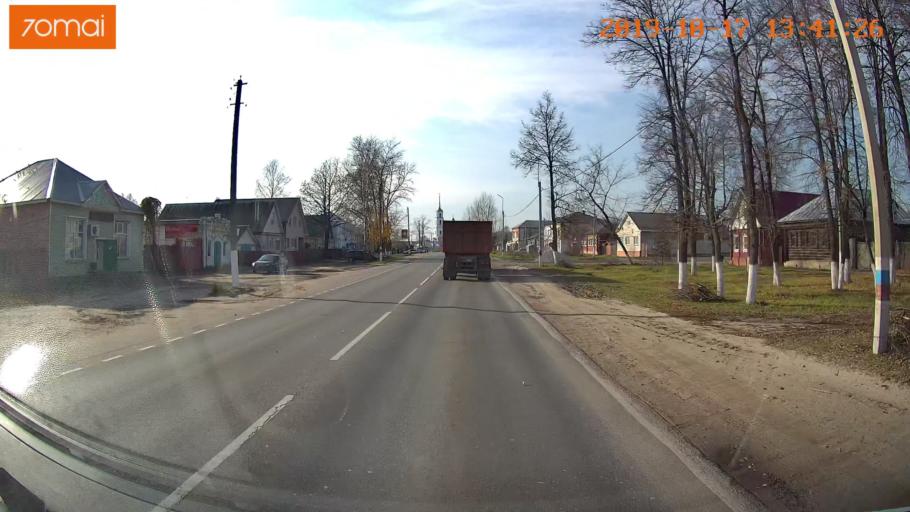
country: RU
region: Rjazan
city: Tuma
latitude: 55.1490
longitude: 40.5644
